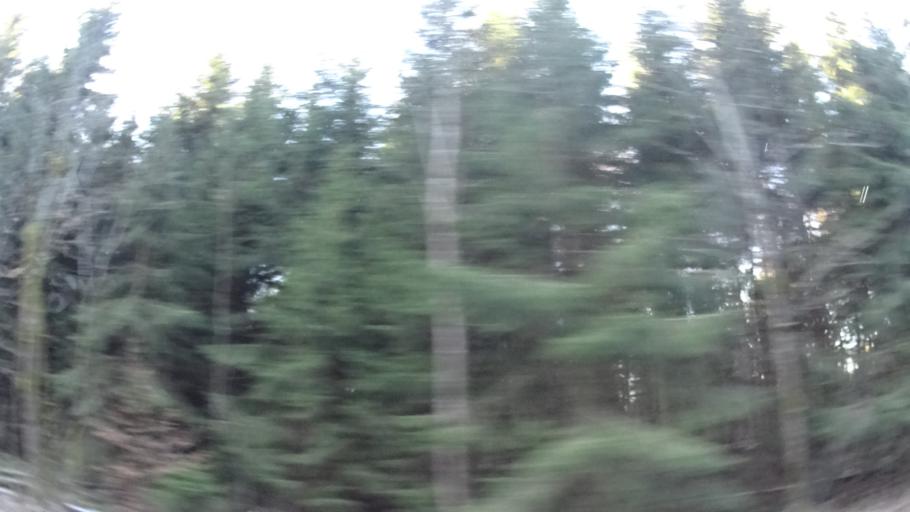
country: DE
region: Thuringia
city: Judenbach
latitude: 50.4222
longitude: 11.2304
